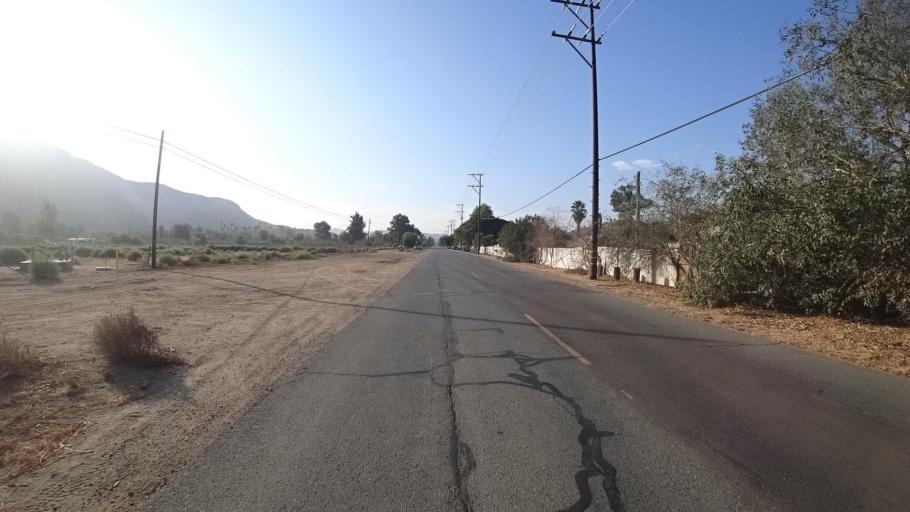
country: US
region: California
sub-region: San Diego County
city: Eucalyptus Hills
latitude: 32.8933
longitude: -116.9279
